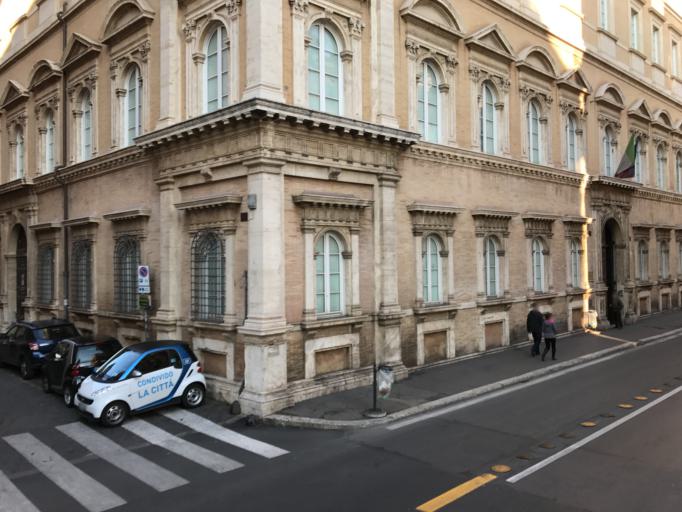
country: VA
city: Vatican City
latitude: 41.8974
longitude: 12.4700
